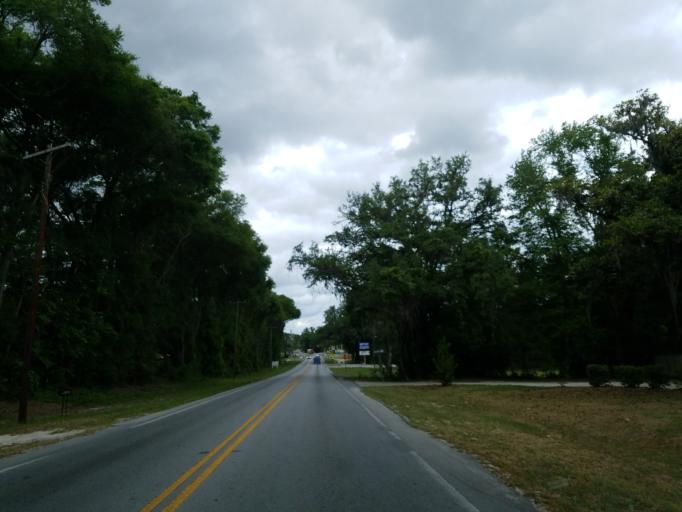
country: US
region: Florida
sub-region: Marion County
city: Ocala
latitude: 29.2855
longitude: -82.1116
